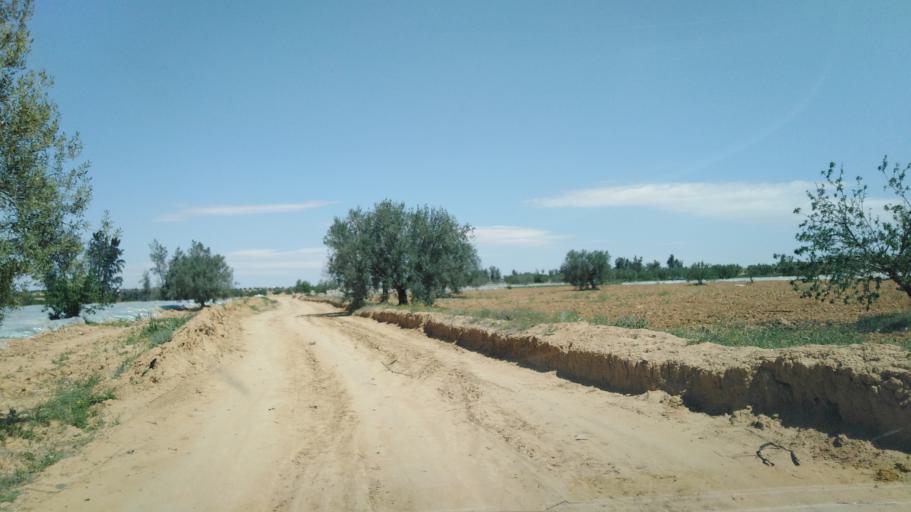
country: TN
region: Safaqis
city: Sfax
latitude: 34.7667
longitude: 10.5279
